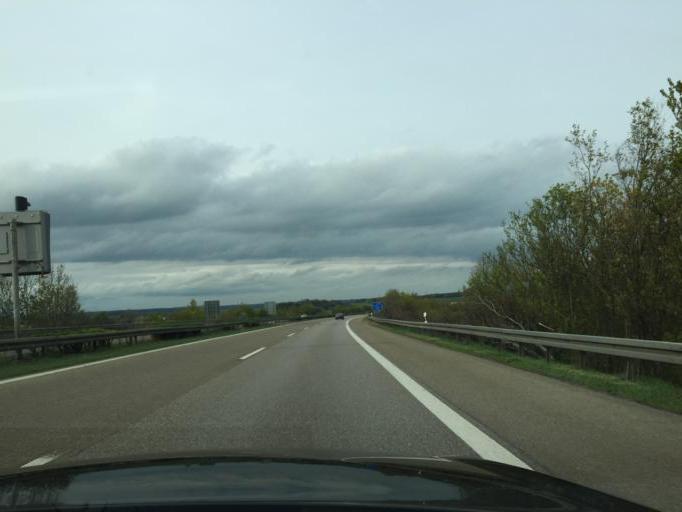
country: DE
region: Baden-Wuerttemberg
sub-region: Regierungsbezirk Stuttgart
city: Westhausen
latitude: 48.8909
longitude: 10.1687
